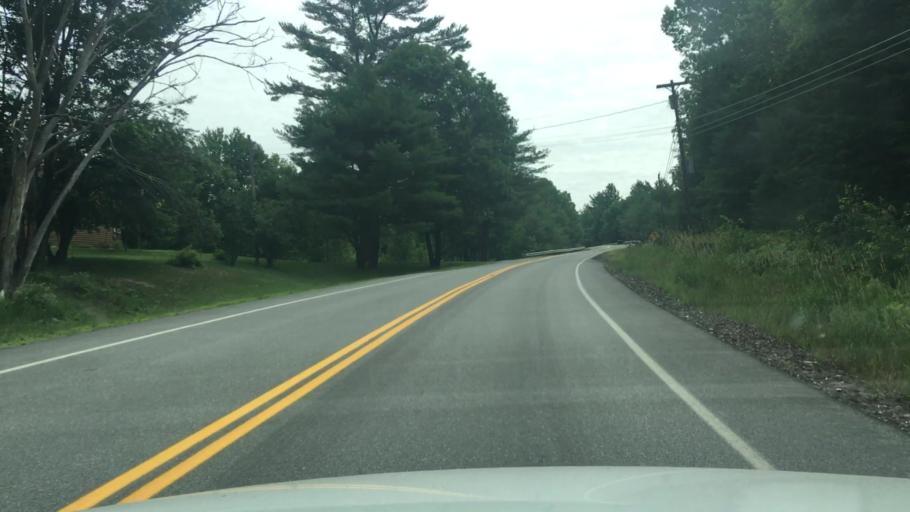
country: US
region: Maine
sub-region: Kennebec County
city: Clinton
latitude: 44.6019
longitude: -69.4670
